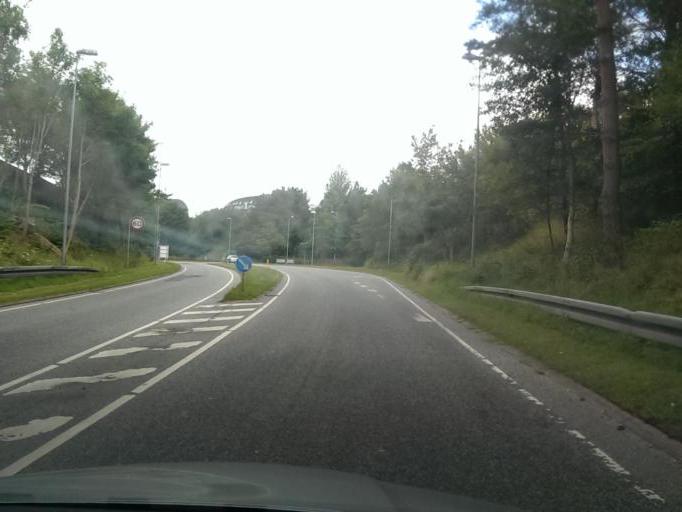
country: DK
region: North Denmark
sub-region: Hjorring Kommune
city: Hjorring
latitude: 57.4591
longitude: 9.9786
